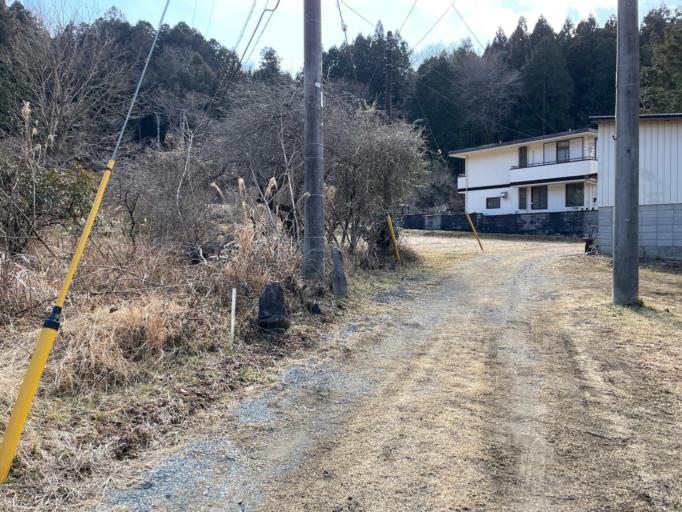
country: JP
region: Saitama
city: Hanno
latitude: 35.8438
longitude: 139.2571
